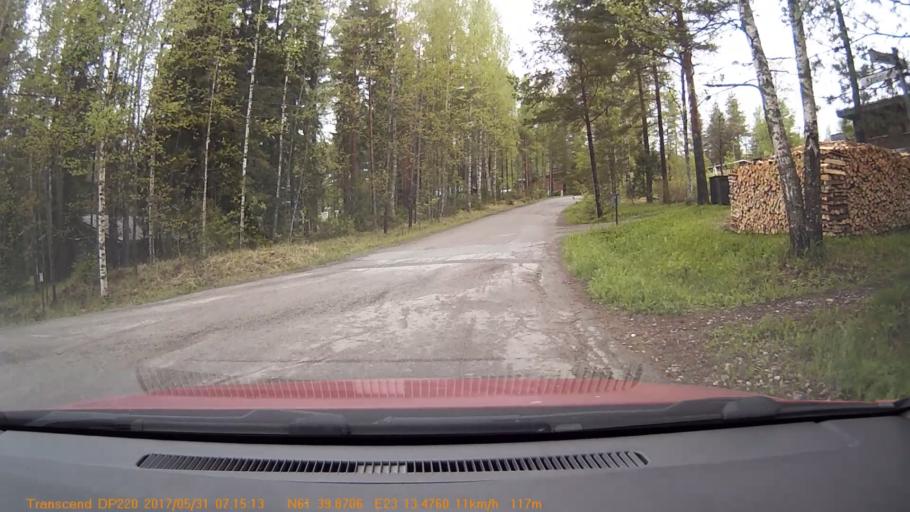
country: FI
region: Pirkanmaa
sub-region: Tampere
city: Haemeenkyroe
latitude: 61.6645
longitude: 23.2246
